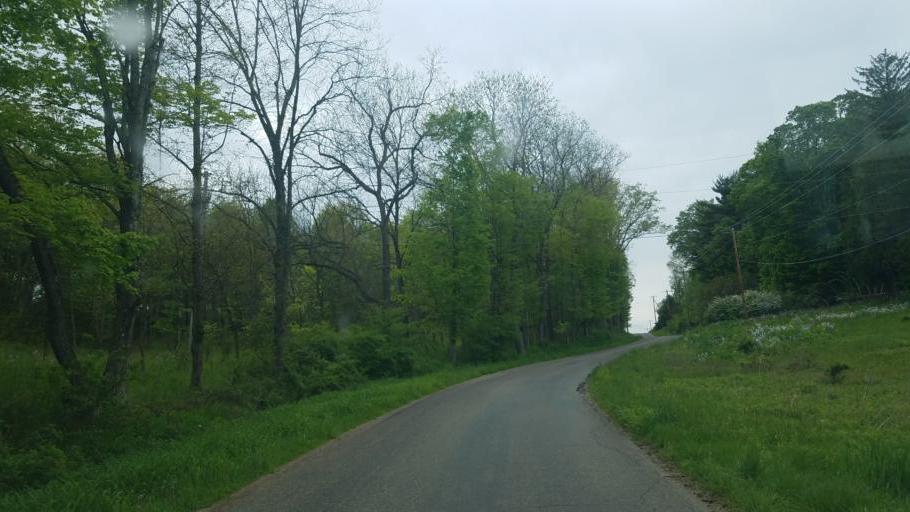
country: US
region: Ohio
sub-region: Knox County
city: Gambier
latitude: 40.3893
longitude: -82.3935
